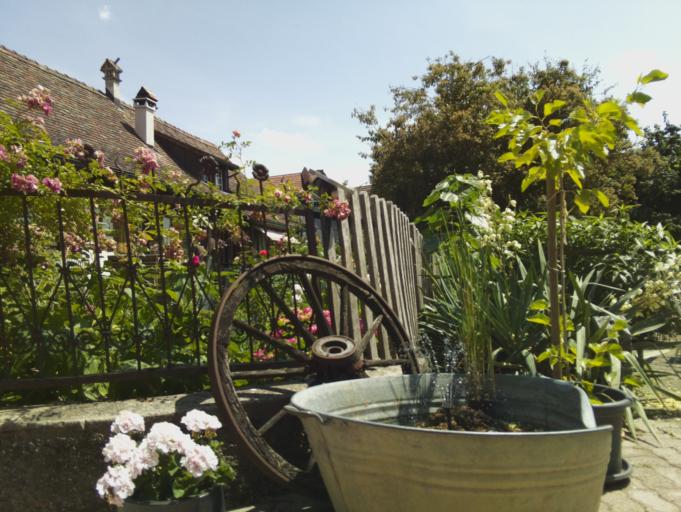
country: CH
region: Zurich
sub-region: Bezirk Andelfingen
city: Marthalen
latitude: 47.6265
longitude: 8.6466
